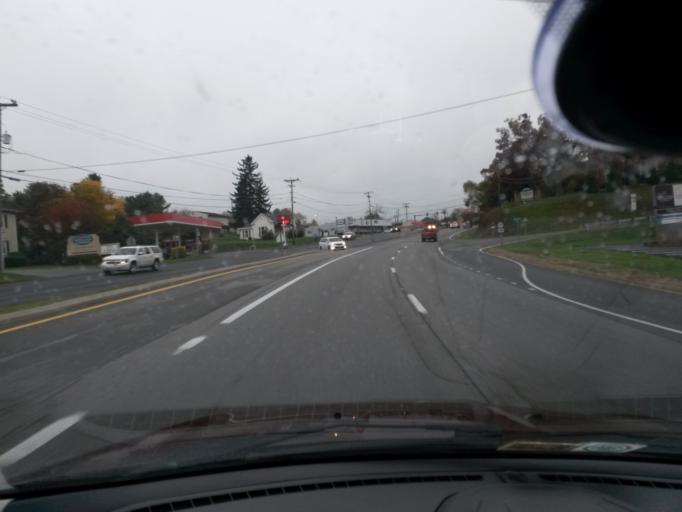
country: US
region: Virginia
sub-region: Botetourt County
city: Daleville
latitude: 37.4079
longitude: -79.9137
